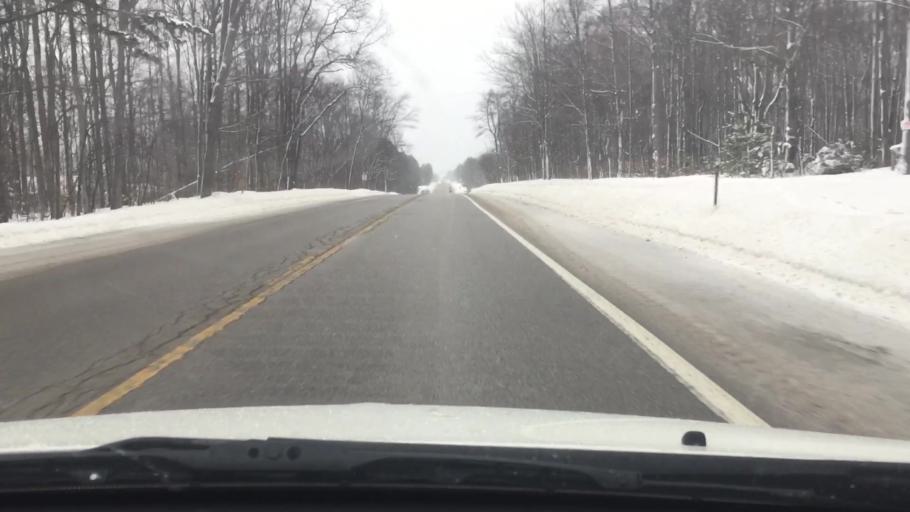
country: US
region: Michigan
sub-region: Otsego County
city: Gaylord
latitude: 45.0359
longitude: -84.7758
